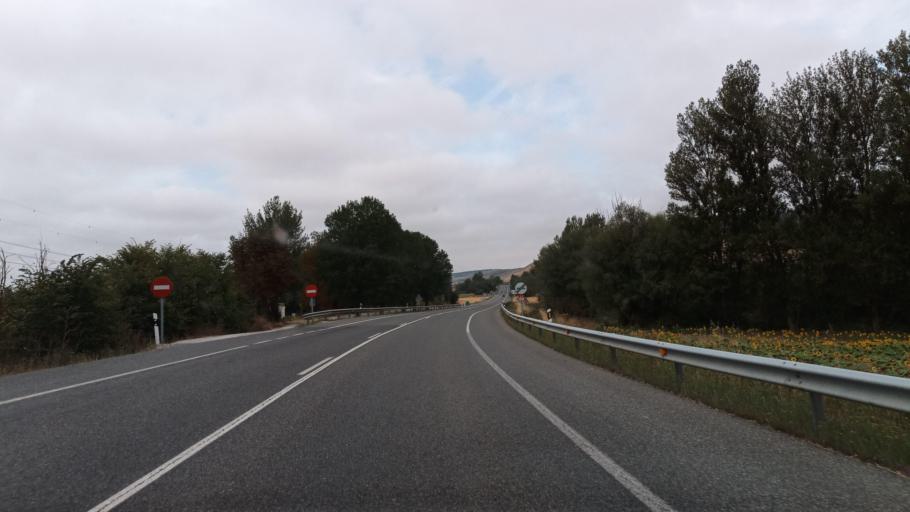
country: ES
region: Castille and Leon
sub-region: Provincia de Burgos
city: Santa Olalla de Bureba
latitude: 42.4661
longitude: -3.4373
